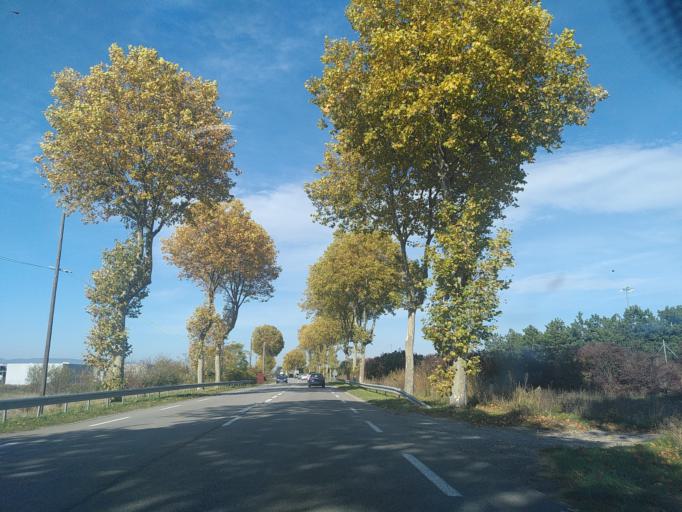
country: FR
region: Rhone-Alpes
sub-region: Departement de la Drome
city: Andancette
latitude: 45.2734
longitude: 4.8237
